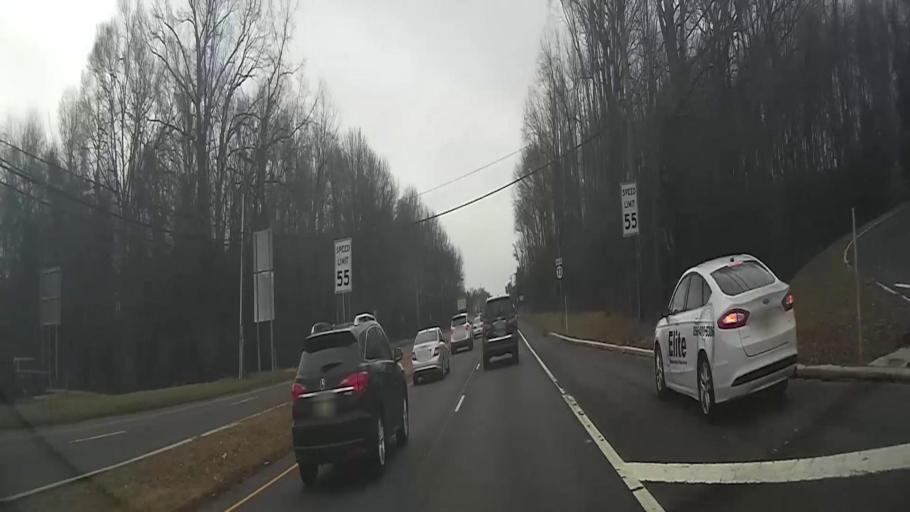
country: US
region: New Jersey
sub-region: Burlington County
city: Marlton
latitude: 39.8742
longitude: -74.9220
